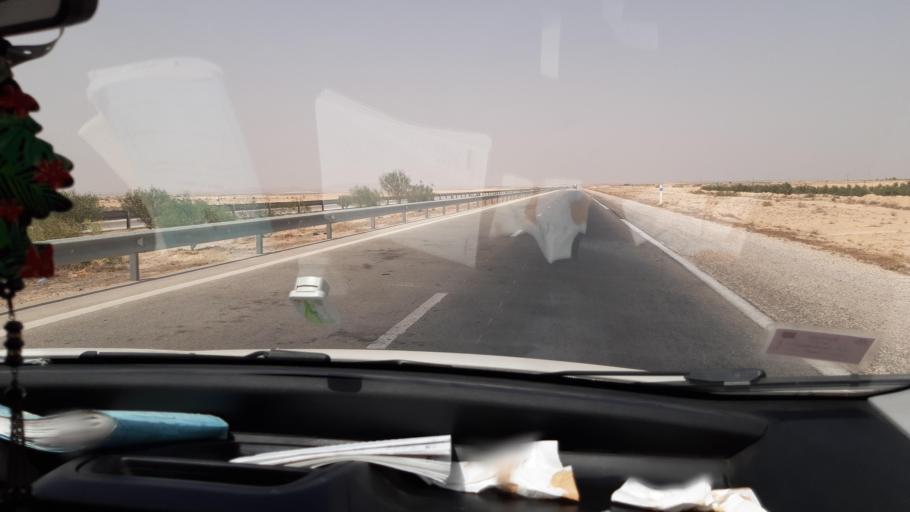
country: TN
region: Qabis
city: Gabes
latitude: 33.9433
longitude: 9.9608
